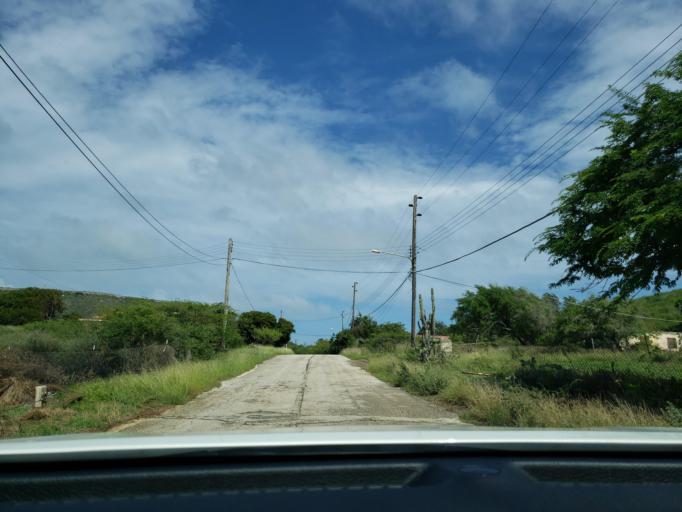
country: CW
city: Barber
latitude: 12.3095
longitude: -69.0898
